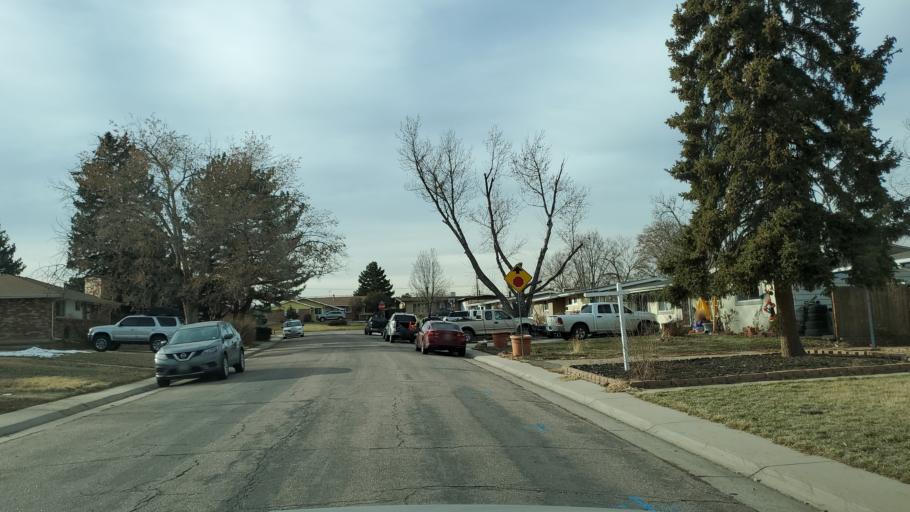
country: US
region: Colorado
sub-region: Adams County
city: Westminster
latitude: 39.8369
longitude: -105.0197
